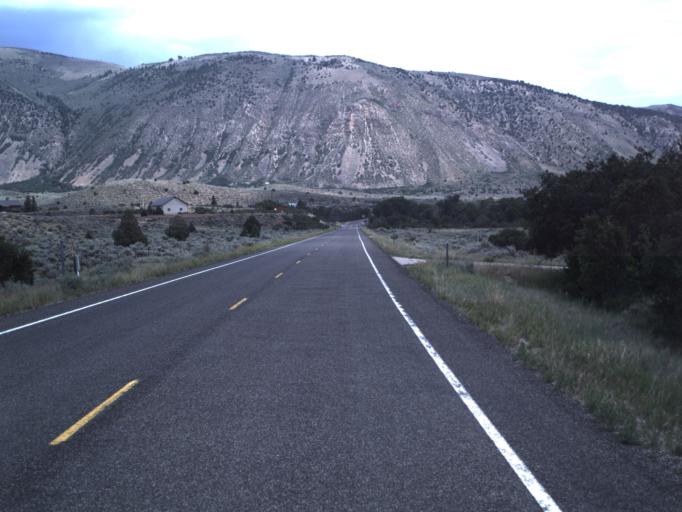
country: US
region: Utah
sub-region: Summit County
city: Francis
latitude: 40.4623
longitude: -110.8400
